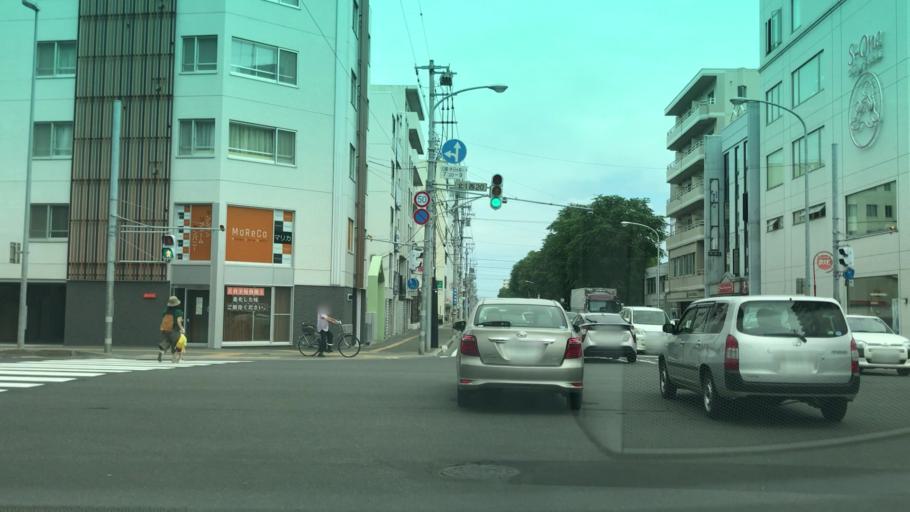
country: JP
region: Hokkaido
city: Sapporo
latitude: 43.0585
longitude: 141.3269
